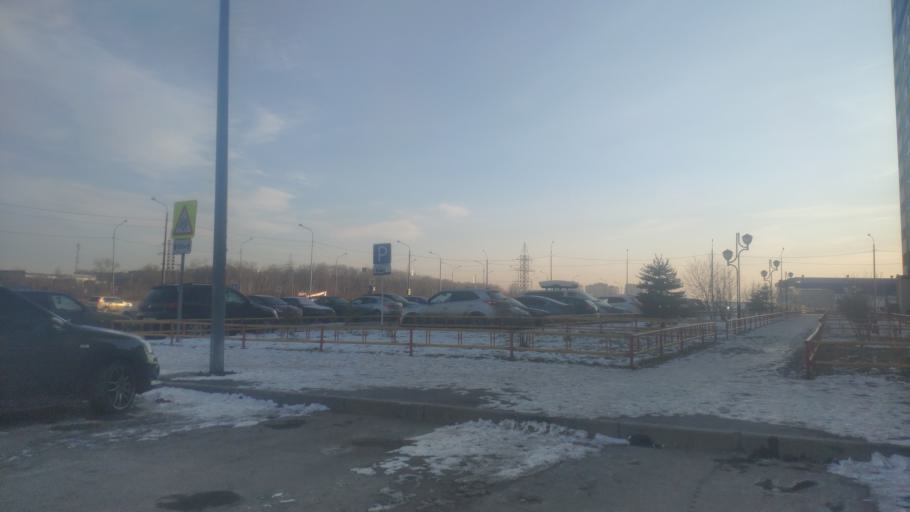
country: RU
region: Tjumen
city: Tyumen
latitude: 57.1778
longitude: 65.5675
